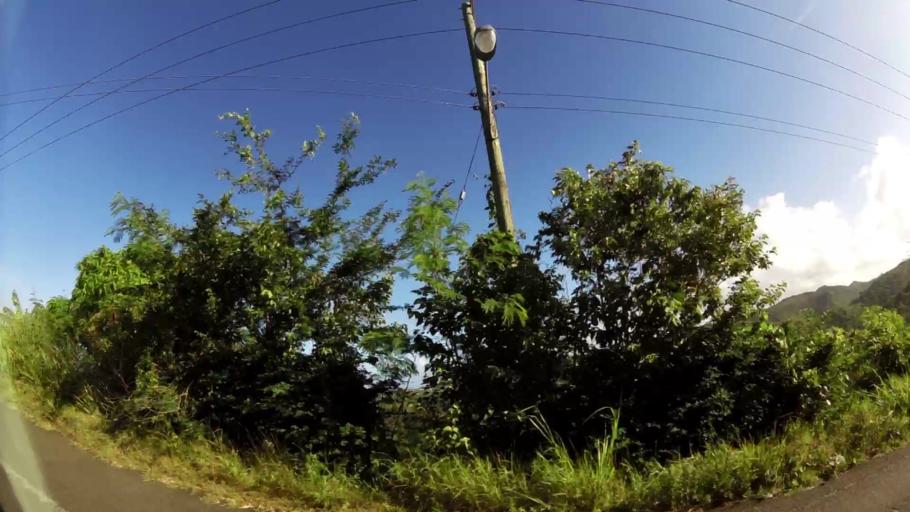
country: LC
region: Anse-la-Raye
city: Anse La Raye
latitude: 13.9251
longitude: -61.0443
